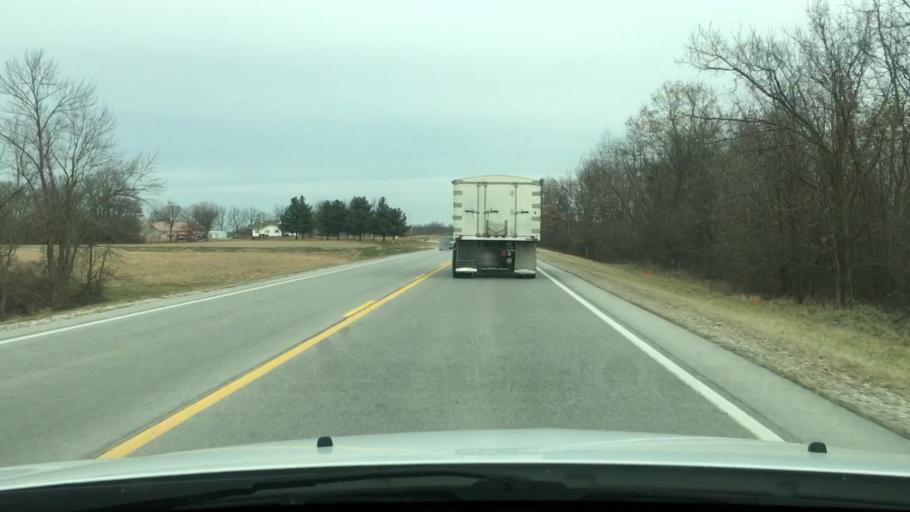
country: US
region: Illinois
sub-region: Pike County
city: Pittsfield
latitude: 39.6583
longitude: -90.7771
